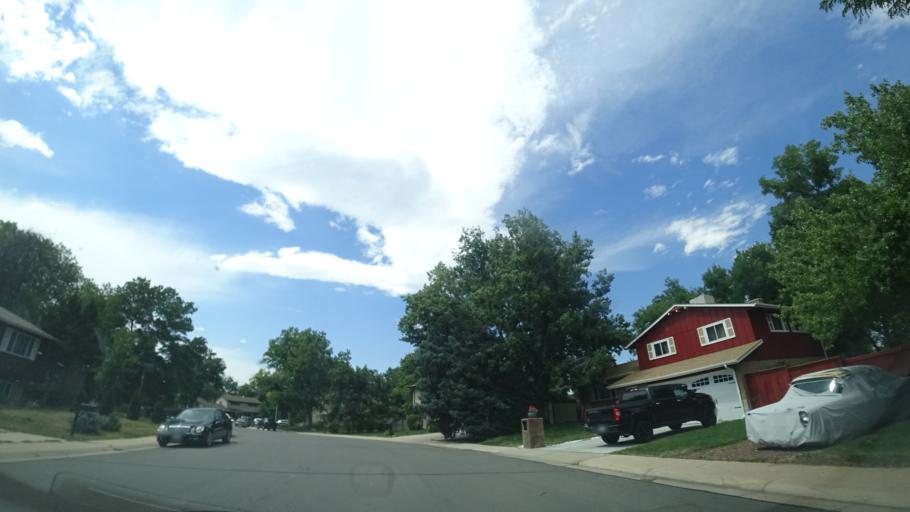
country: US
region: Colorado
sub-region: Jefferson County
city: Lakewood
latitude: 39.6942
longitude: -105.1081
